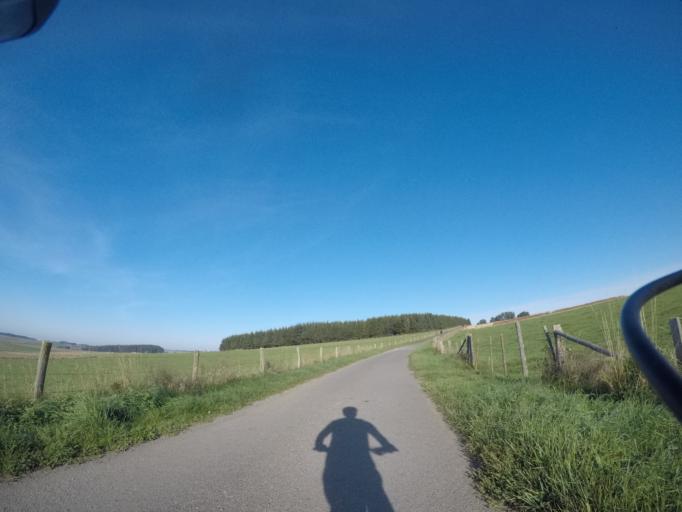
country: BE
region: Wallonia
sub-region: Province du Luxembourg
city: Bastogne
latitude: 49.9670
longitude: 5.7106
